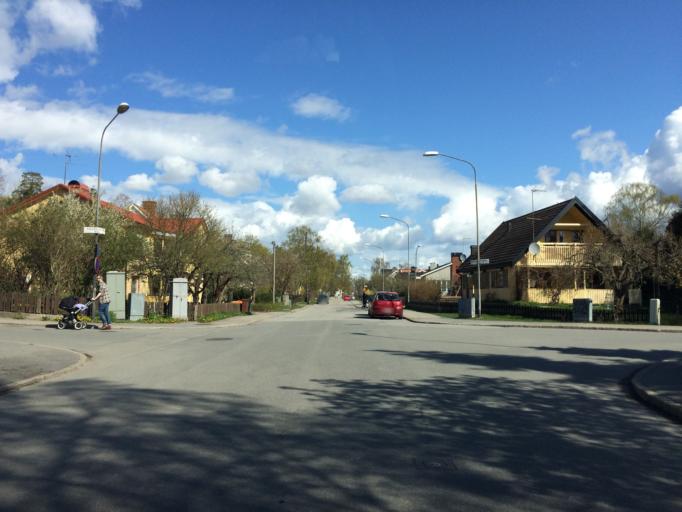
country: SE
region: Stockholm
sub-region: Huddinge Kommun
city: Segeltorp
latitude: 59.2961
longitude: 17.9479
